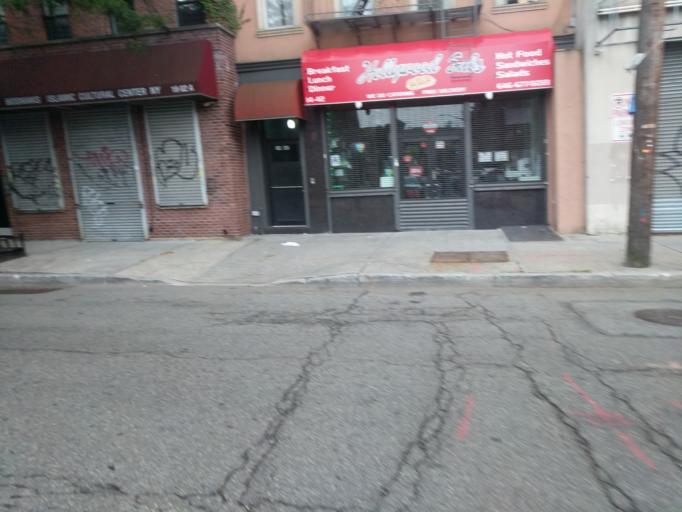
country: US
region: New York
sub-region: Queens County
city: Long Island City
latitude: 40.7723
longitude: -73.9274
